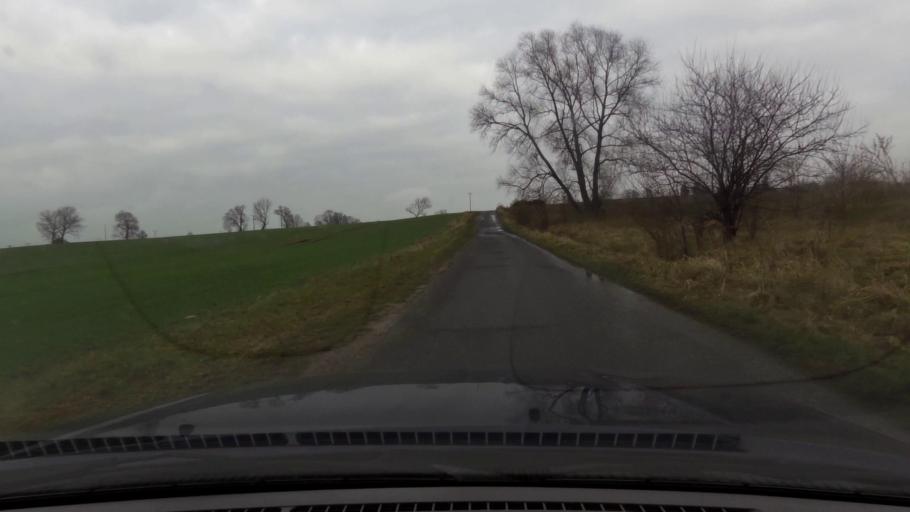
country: PL
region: West Pomeranian Voivodeship
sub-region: Powiat stargardzki
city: Stara Dabrowa
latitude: 53.3481
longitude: 15.1281
